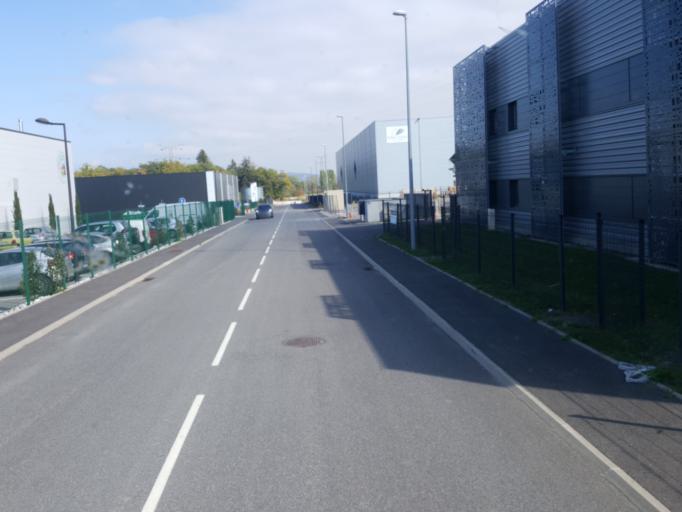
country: FR
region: Rhone-Alpes
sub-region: Departement de la Haute-Savoie
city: Ballaison
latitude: 46.2768
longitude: 6.3444
